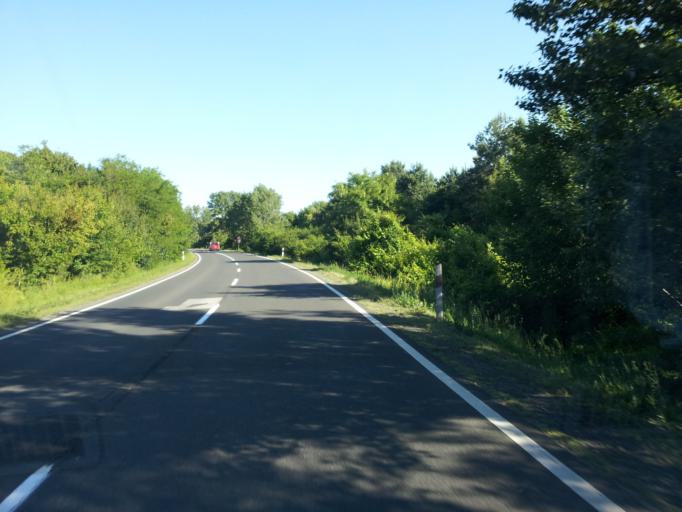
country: HU
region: Nograd
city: Nagyoroszi
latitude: 48.0450
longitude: 19.0473
